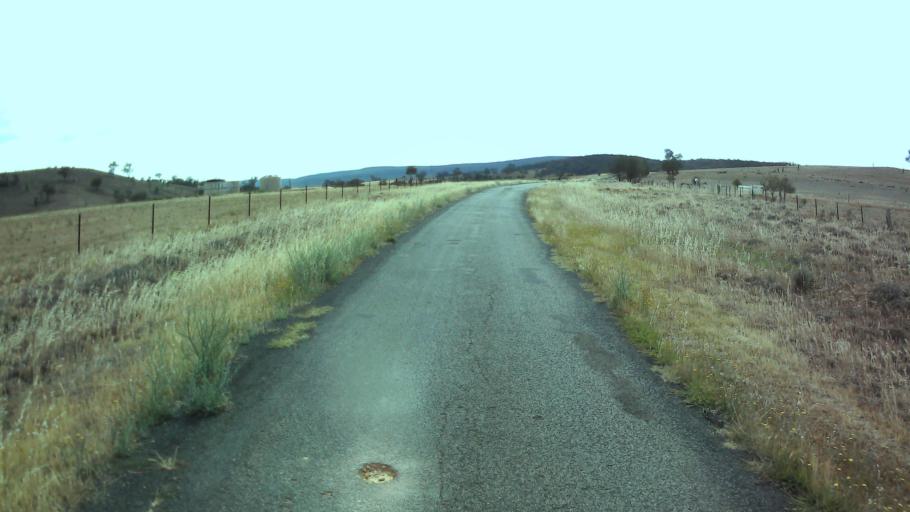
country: AU
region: New South Wales
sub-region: Weddin
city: Grenfell
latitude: -33.8439
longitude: 148.2536
